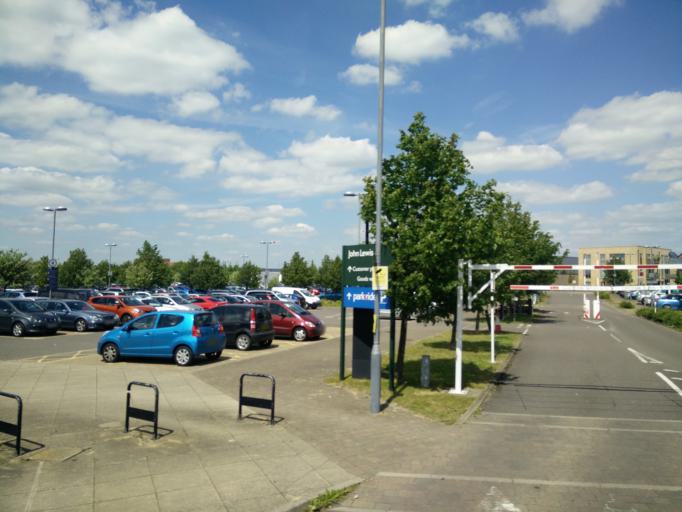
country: GB
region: England
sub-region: Cambridgeshire
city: Grantchester
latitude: 52.1679
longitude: 0.1084
